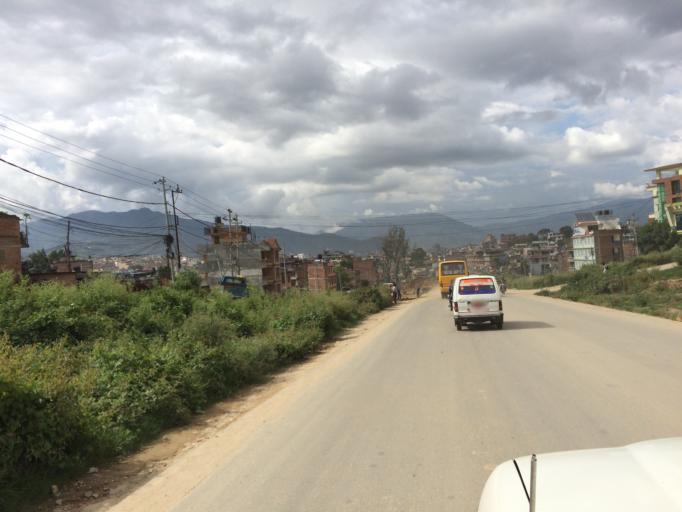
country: NP
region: Central Region
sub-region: Bagmati Zone
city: Patan
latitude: 27.6805
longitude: 85.3023
